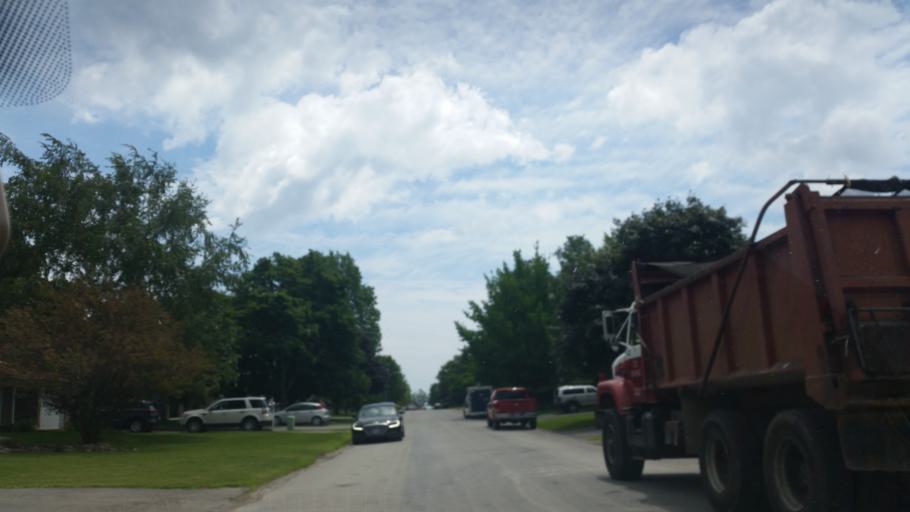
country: CA
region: Ontario
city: Norfolk County
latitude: 42.7915
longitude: -80.1809
